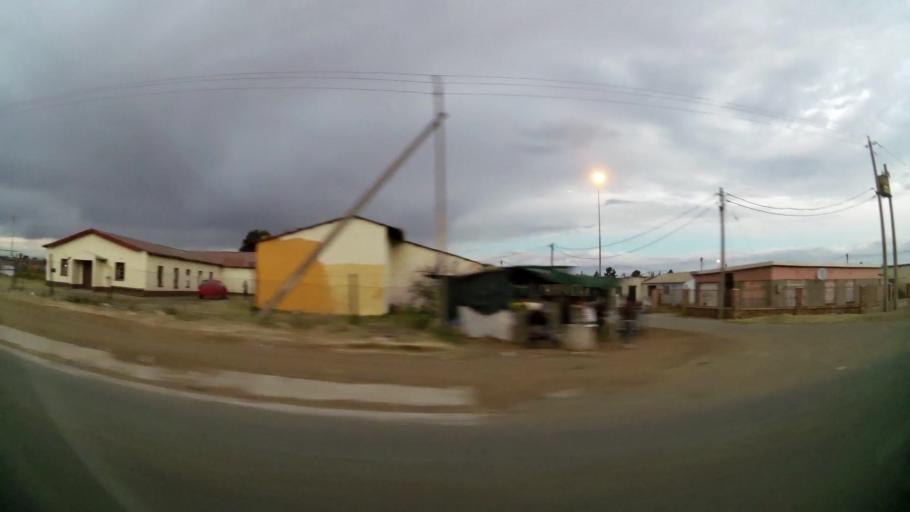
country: ZA
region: Orange Free State
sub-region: Lejweleputswa District Municipality
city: Welkom
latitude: -27.9603
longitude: 26.7855
